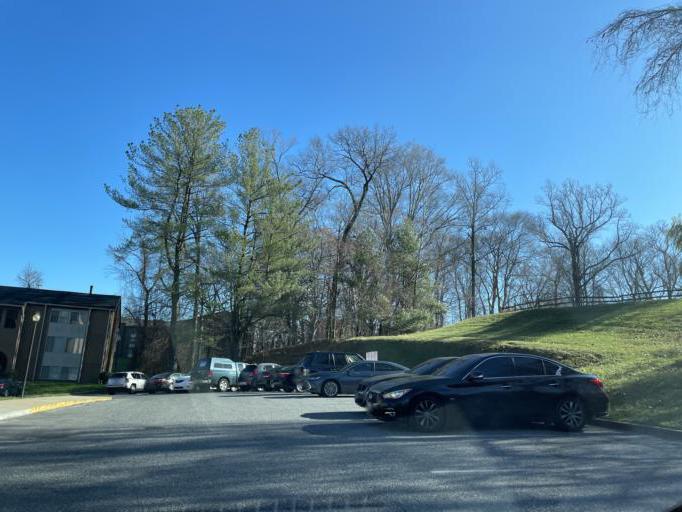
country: US
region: Maryland
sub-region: Baltimore County
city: Mays Chapel
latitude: 39.3806
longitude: -76.6641
